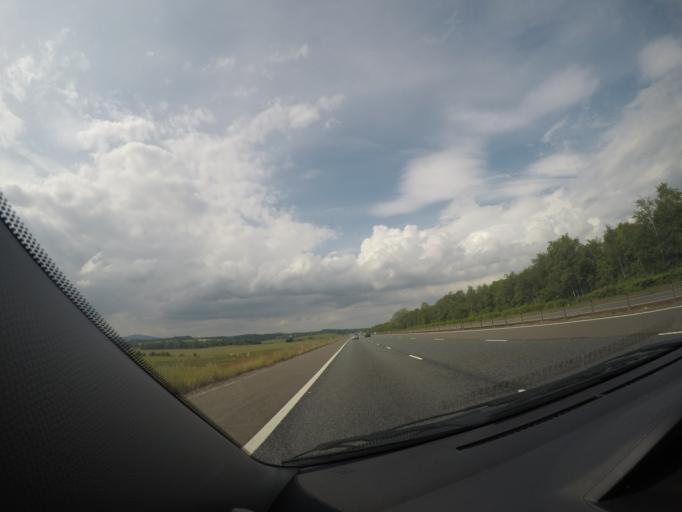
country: GB
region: Scotland
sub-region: Dumfries and Galloway
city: Lochmaben
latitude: 55.1914
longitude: -3.4088
